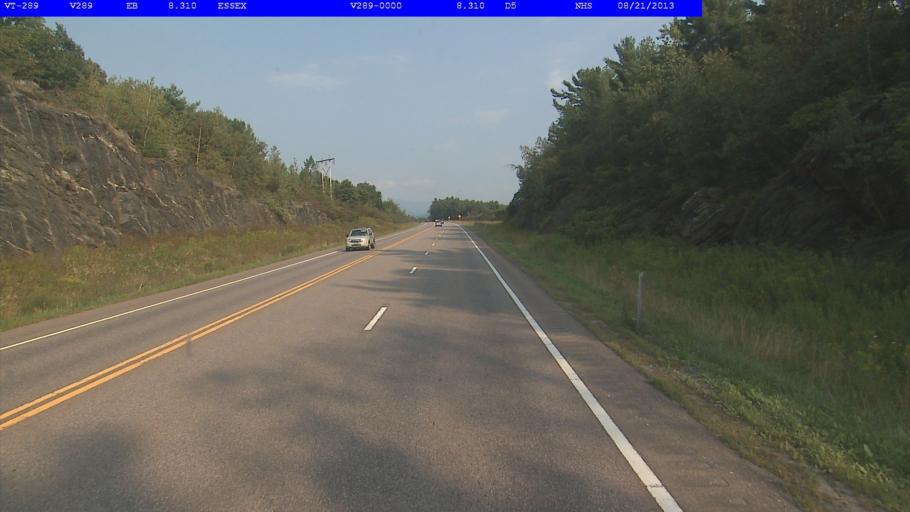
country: US
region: Vermont
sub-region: Chittenden County
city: Essex Junction
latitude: 44.5155
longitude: -73.1077
